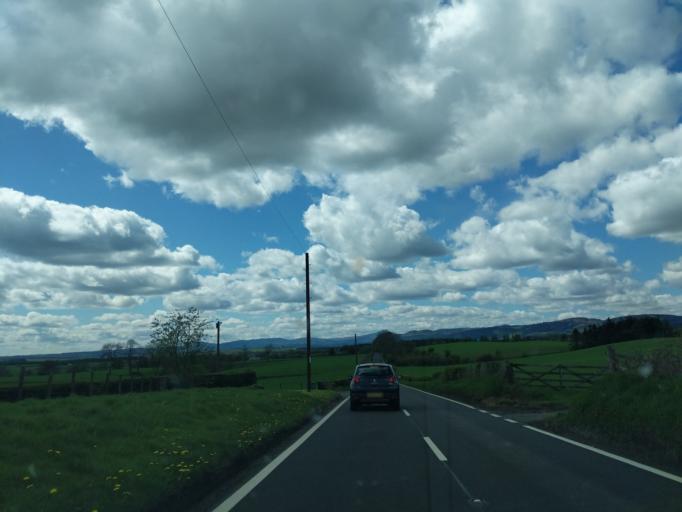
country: GB
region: Scotland
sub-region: Stirling
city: Doune
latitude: 56.1715
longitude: -4.1261
